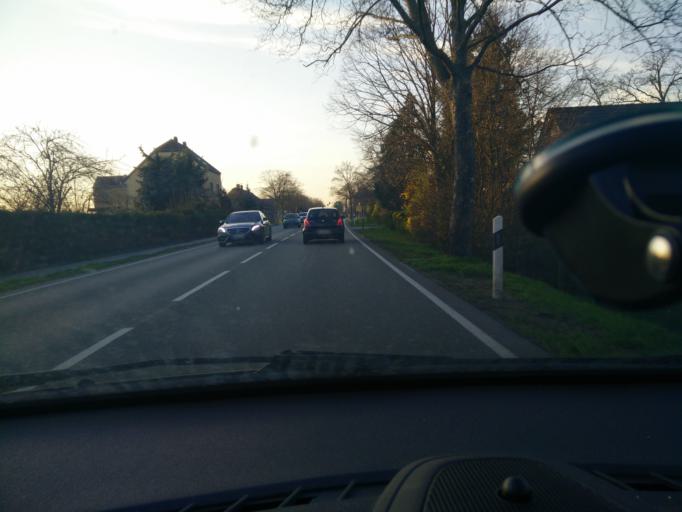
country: DE
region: North Rhine-Westphalia
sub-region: Regierungsbezirk Dusseldorf
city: Moers
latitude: 51.5016
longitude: 6.6241
